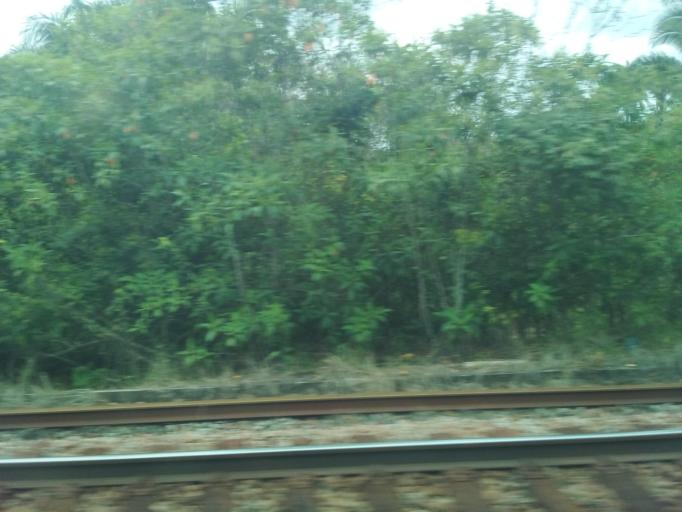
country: BR
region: Maranhao
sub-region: Santa Ines
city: Santa Ines
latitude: -3.6525
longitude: -45.7952
